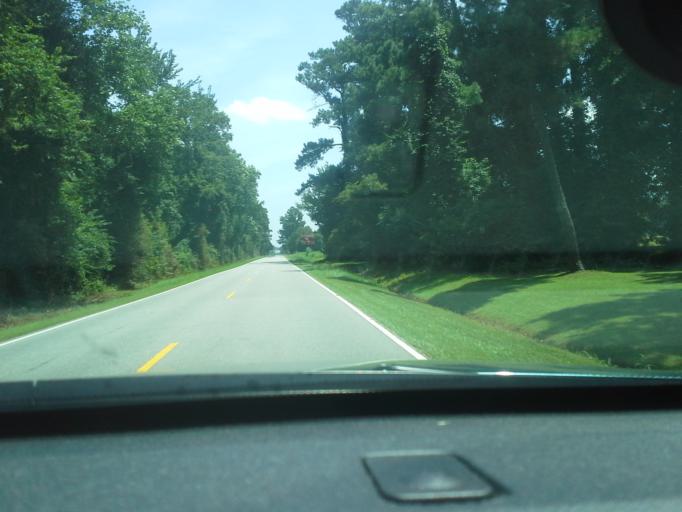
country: US
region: North Carolina
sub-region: Washington County
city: Plymouth
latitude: 35.9224
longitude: -76.6359
